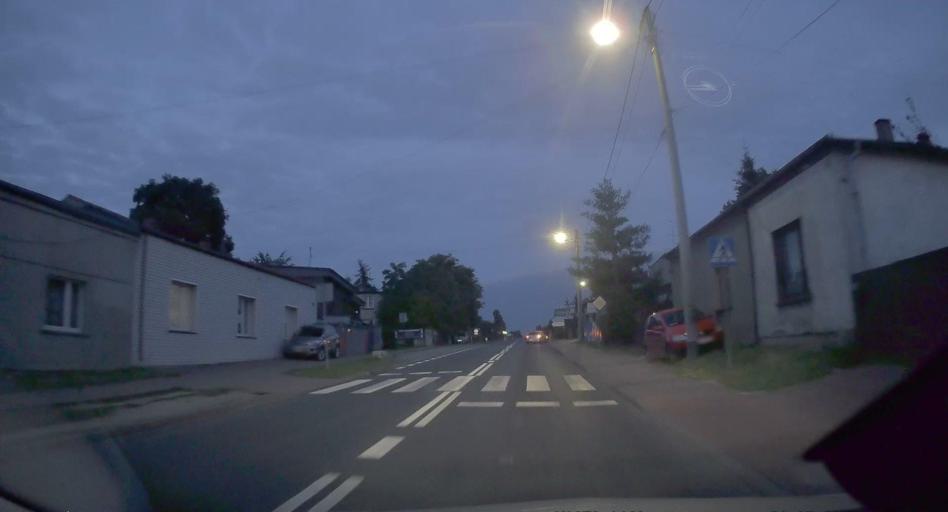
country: PL
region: Silesian Voivodeship
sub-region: Powiat klobucki
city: Klobuck
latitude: 50.8995
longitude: 18.9407
